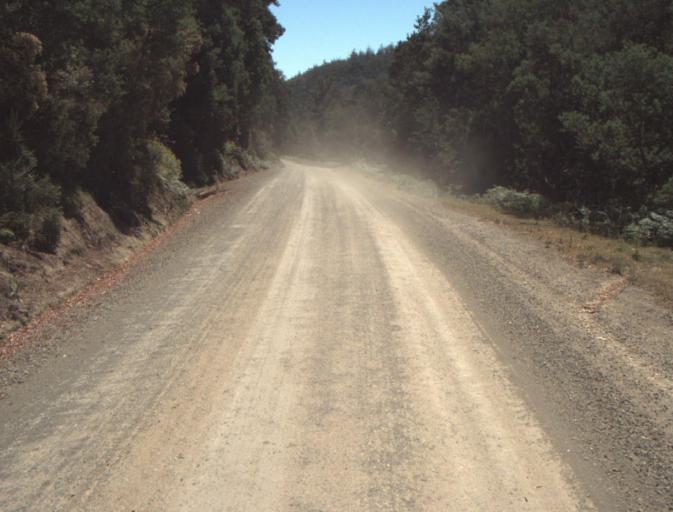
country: AU
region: Tasmania
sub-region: Dorset
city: Scottsdale
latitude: -41.3250
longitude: 147.4216
